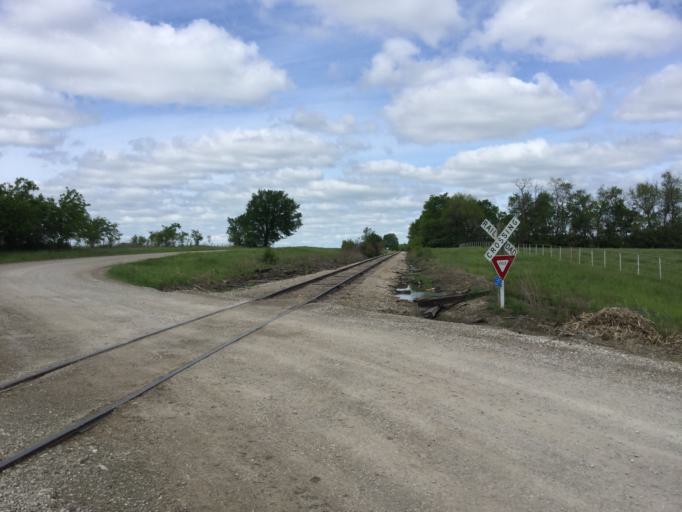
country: US
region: Kansas
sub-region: Labette County
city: Altamont
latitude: 37.2081
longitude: -95.4181
